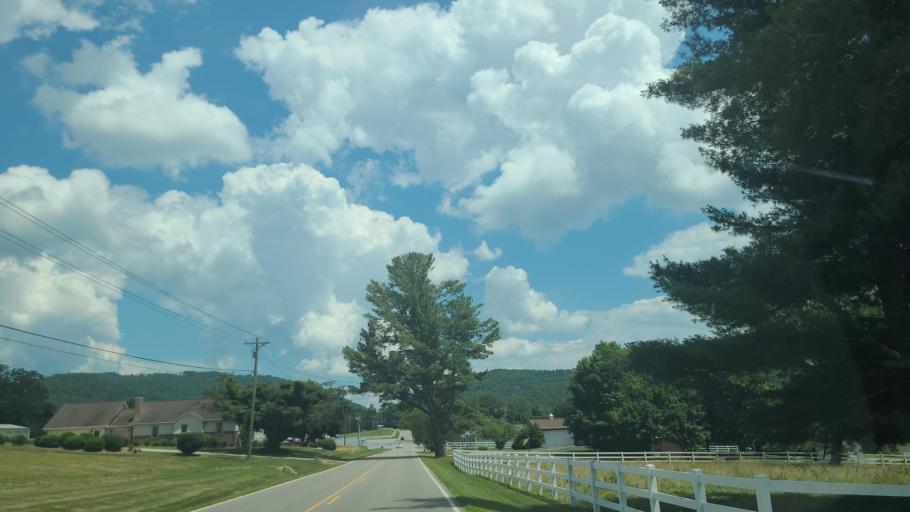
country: US
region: North Carolina
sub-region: Watauga County
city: Boone
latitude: 36.2401
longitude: -81.5257
